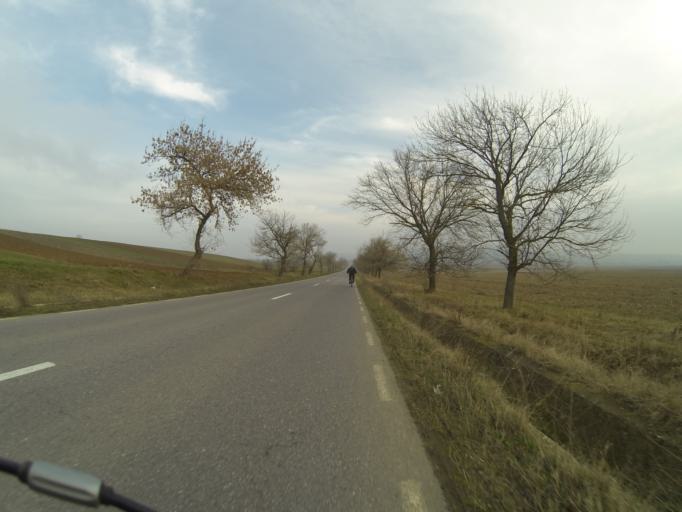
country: RO
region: Mehedinti
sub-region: Comuna Corlatel
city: Corlatel
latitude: 44.3998
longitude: 22.9150
